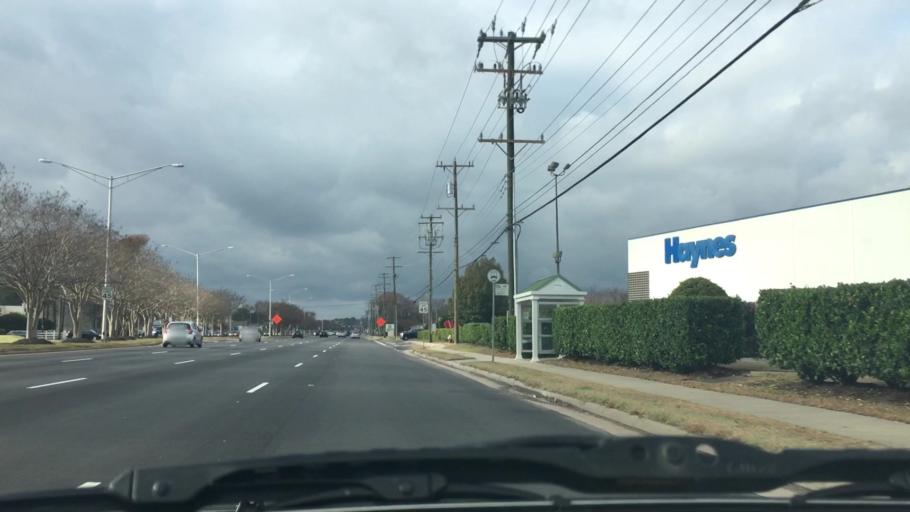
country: US
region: Virginia
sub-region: City of Chesapeake
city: Chesapeake
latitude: 36.8491
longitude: -76.1646
